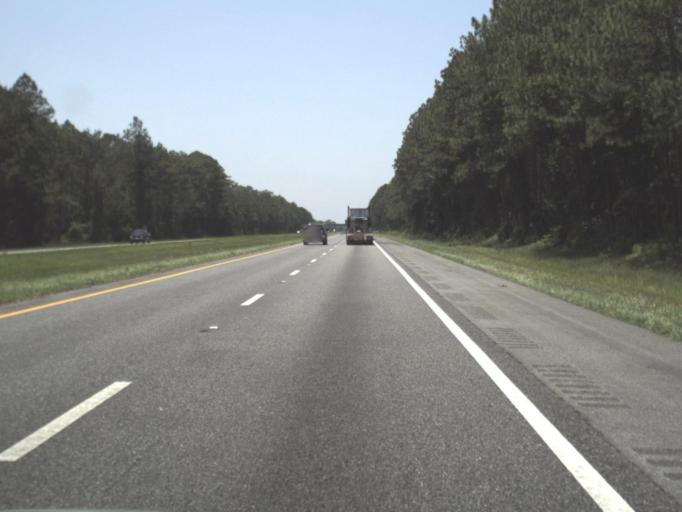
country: US
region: Florida
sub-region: Union County
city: Lake Butler
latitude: 30.2545
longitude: -82.3829
